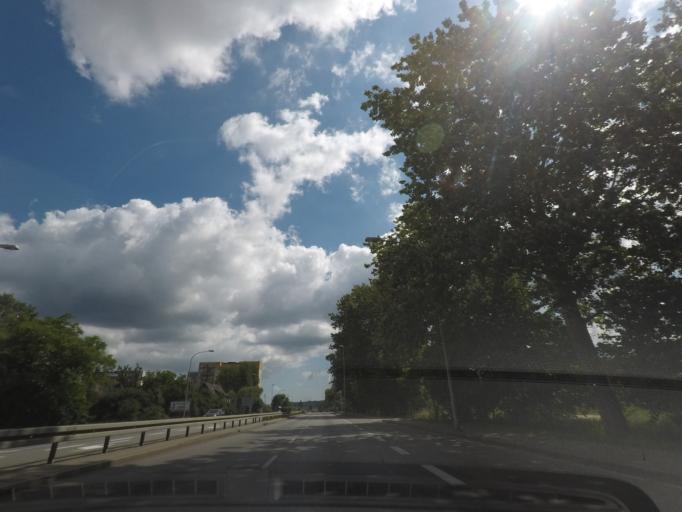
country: PL
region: Pomeranian Voivodeship
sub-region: Powiat wejherowski
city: Wejherowo
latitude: 54.6046
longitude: 18.2436
